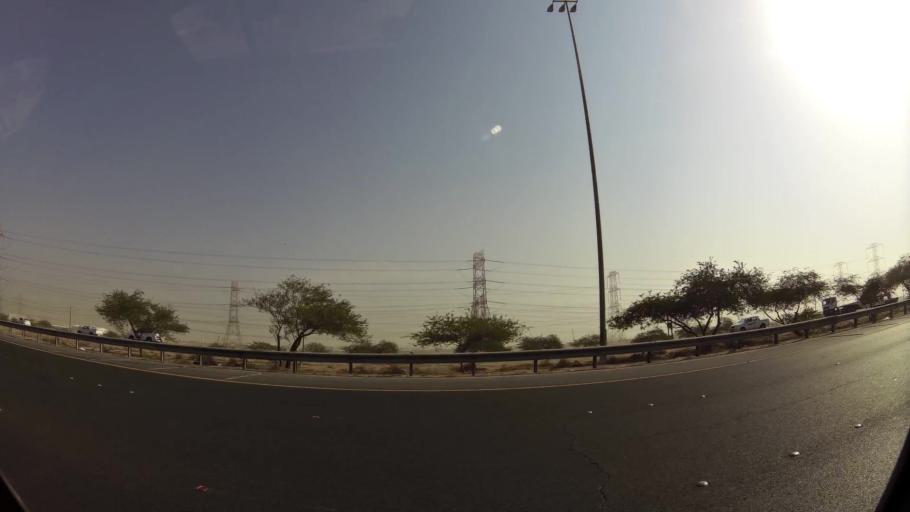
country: KW
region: Al Ahmadi
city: Al Ahmadi
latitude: 28.9987
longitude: 48.0978
